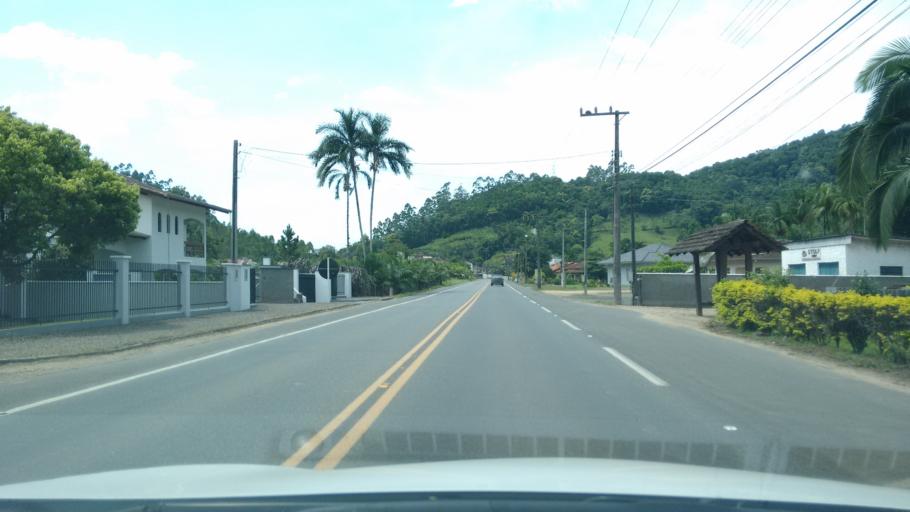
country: BR
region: Santa Catarina
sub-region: Rodeio
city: Gavea
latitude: -26.9003
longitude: -49.3563
